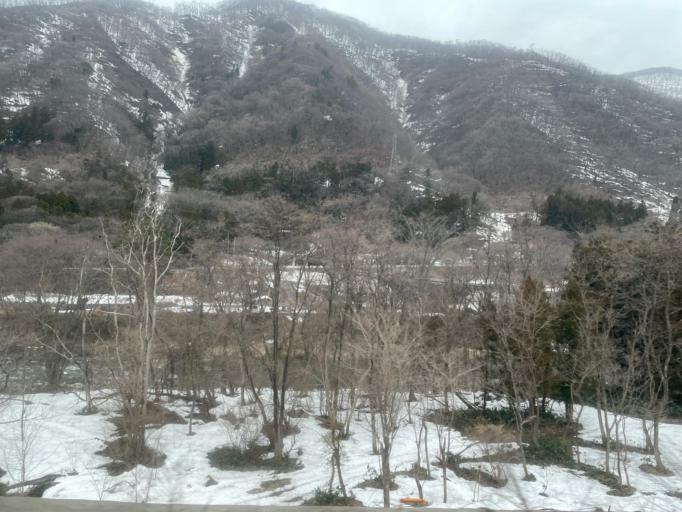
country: JP
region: Gunma
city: Numata
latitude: 36.7875
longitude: 138.9804
